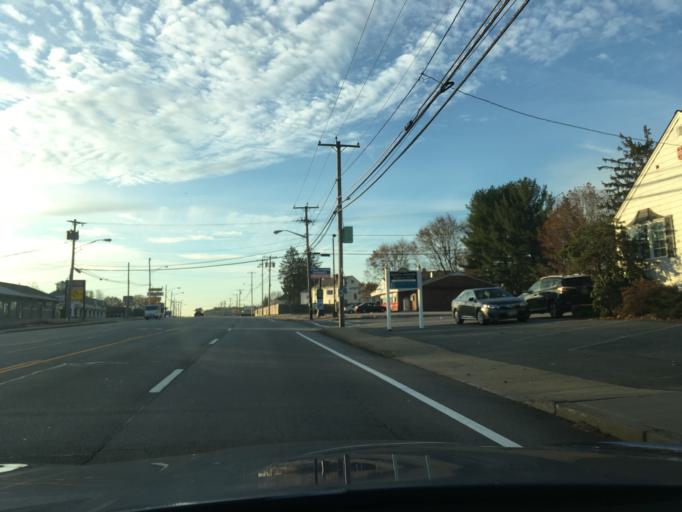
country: US
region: Rhode Island
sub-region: Kent County
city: East Greenwich
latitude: 41.6143
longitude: -71.4578
